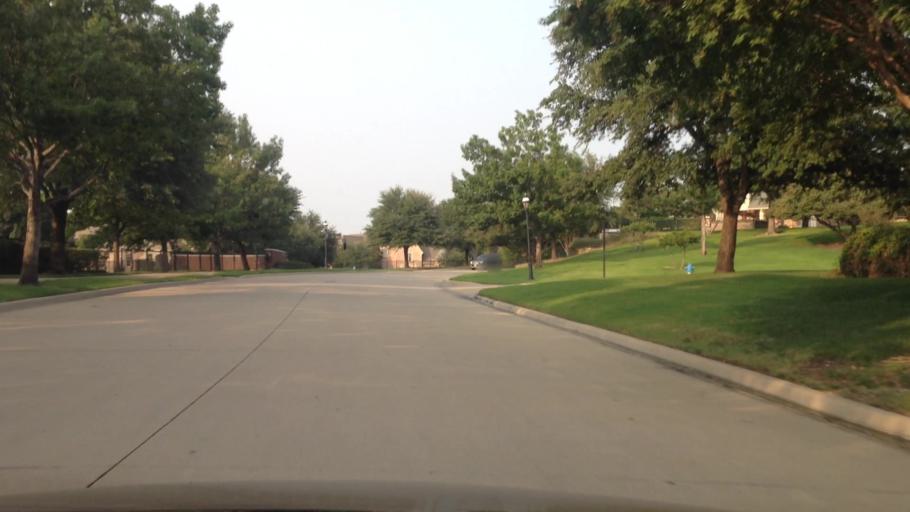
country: US
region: Texas
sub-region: Collin County
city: Frisco
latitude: 33.1278
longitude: -96.8352
